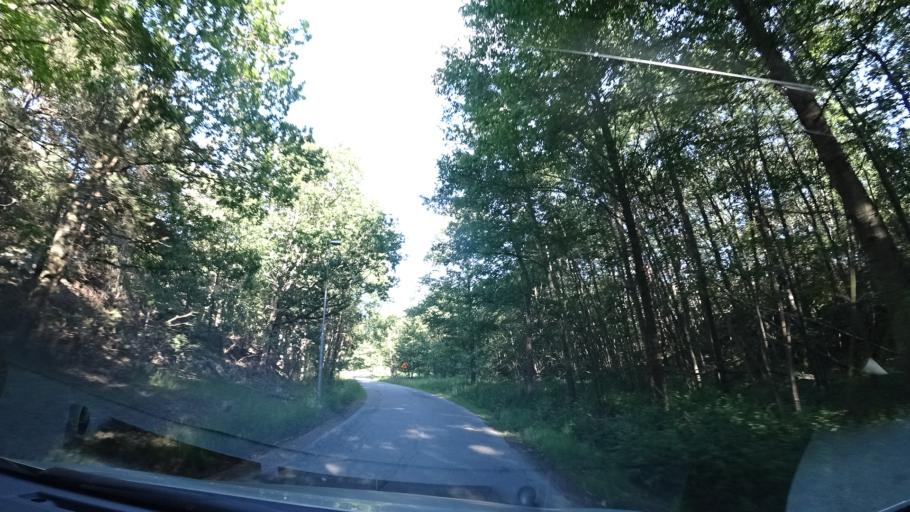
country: SE
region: Vaestra Goetaland
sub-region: Goteborg
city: Billdal
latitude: 57.5824
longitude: 11.9816
